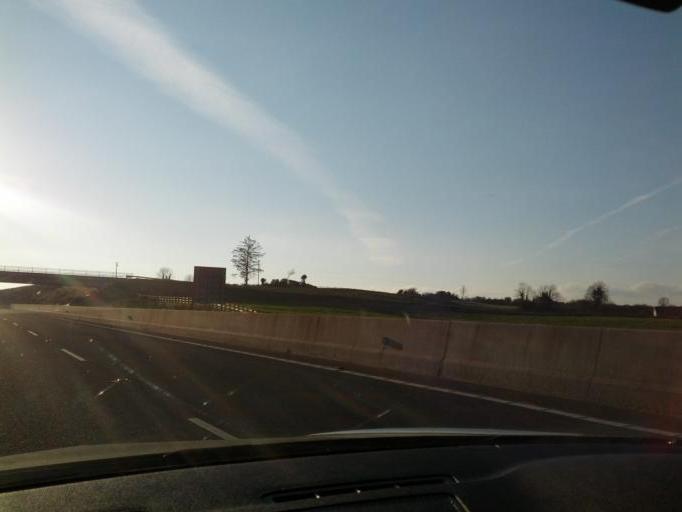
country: IE
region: Munster
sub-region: North Tipperary
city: Roscrea
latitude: 52.9154
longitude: -7.8196
